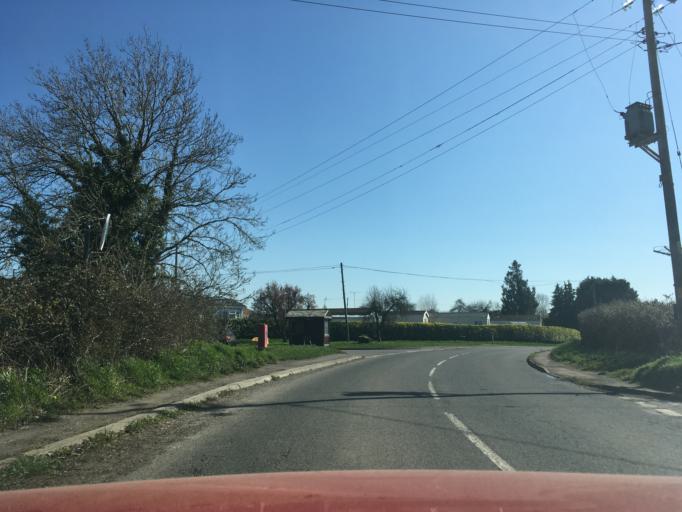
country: GB
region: England
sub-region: Gloucestershire
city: Berkeley
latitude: 51.6943
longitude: -2.4704
